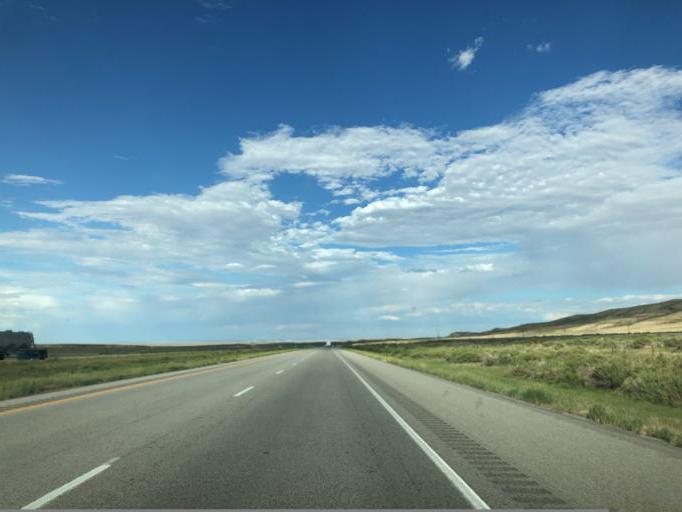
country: US
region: Wyoming
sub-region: Sweetwater County
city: Rock Springs
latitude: 41.6384
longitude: -108.2271
